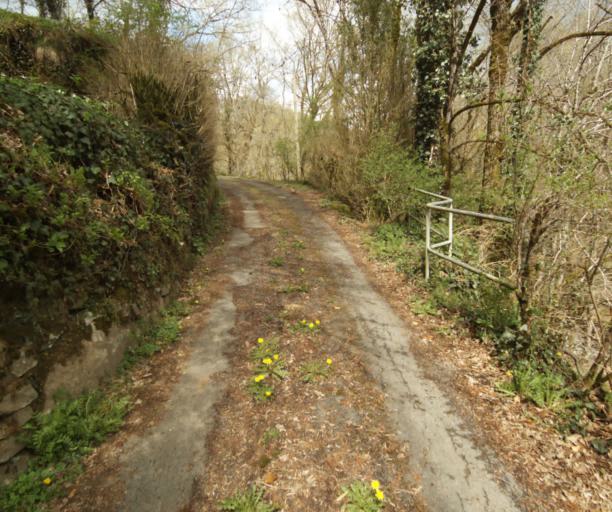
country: FR
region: Limousin
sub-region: Departement de la Correze
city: Tulle
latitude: 45.2718
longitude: 1.7966
